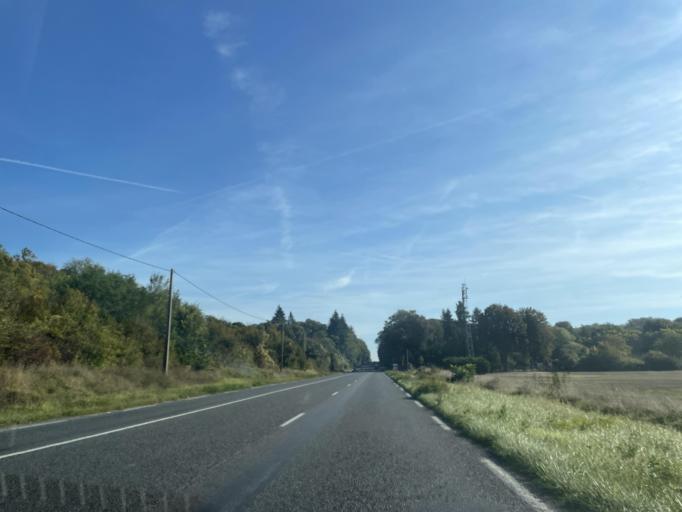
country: FR
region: Ile-de-France
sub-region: Departement de Seine-et-Marne
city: Trilport
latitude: 48.9584
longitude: 2.9700
